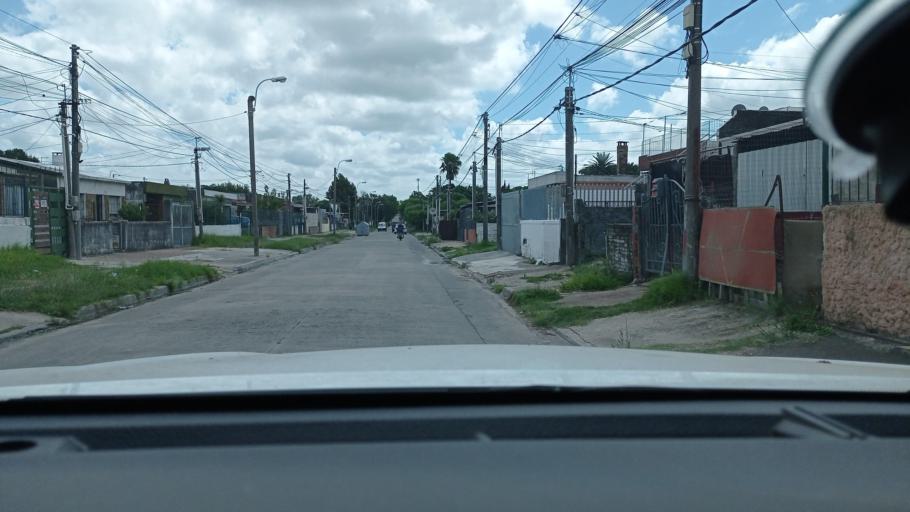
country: UY
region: Canelones
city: La Paz
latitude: -34.8211
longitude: -56.2243
